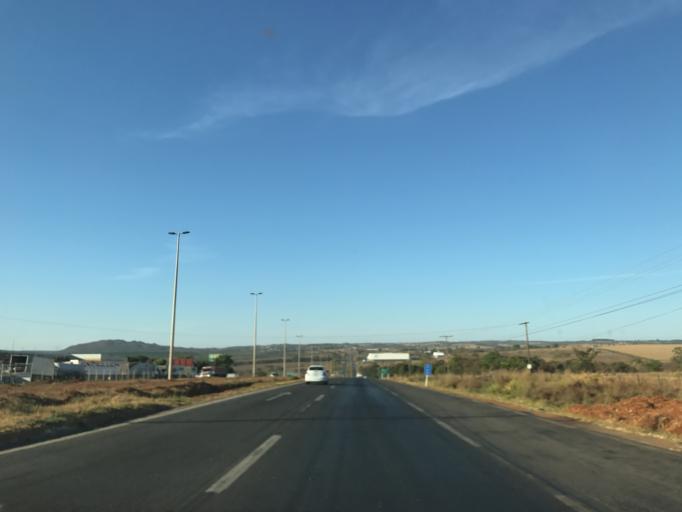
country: BR
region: Goias
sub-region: Aparecida De Goiania
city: Aparecida de Goiania
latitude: -16.8403
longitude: -49.2451
